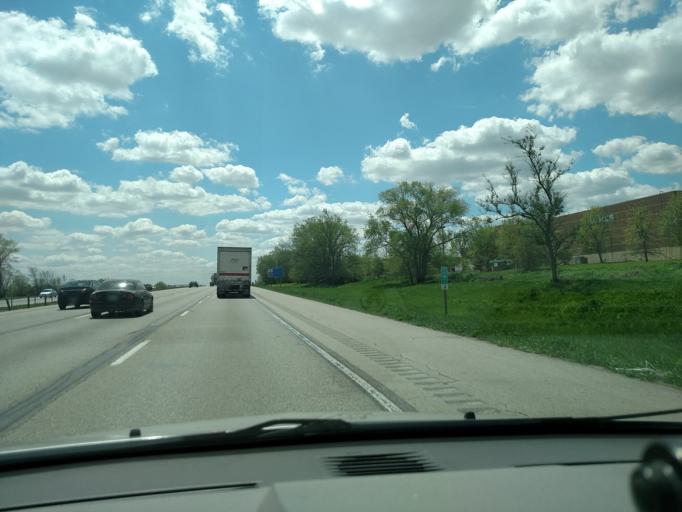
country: US
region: Iowa
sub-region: Polk County
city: Ankeny
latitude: 41.7125
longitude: -93.5766
